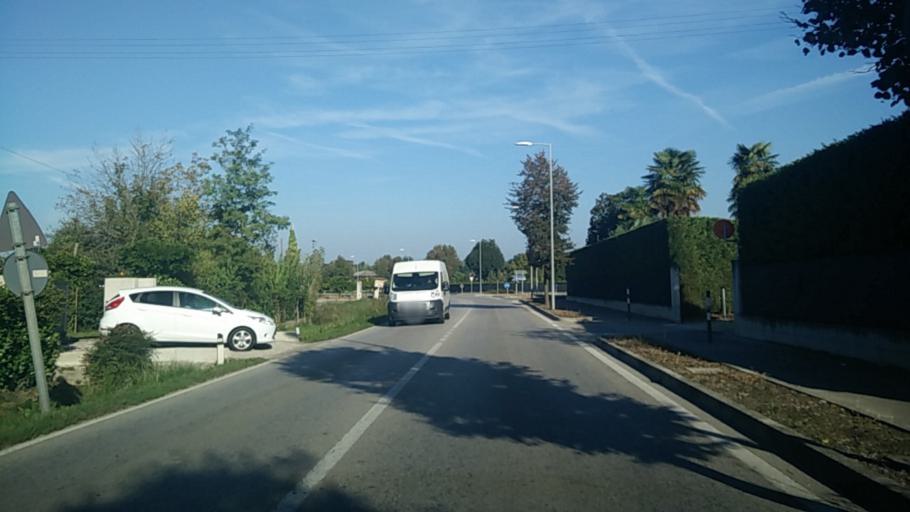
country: IT
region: Veneto
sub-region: Provincia di Padova
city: Trebaseleghe
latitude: 45.6051
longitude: 12.0277
